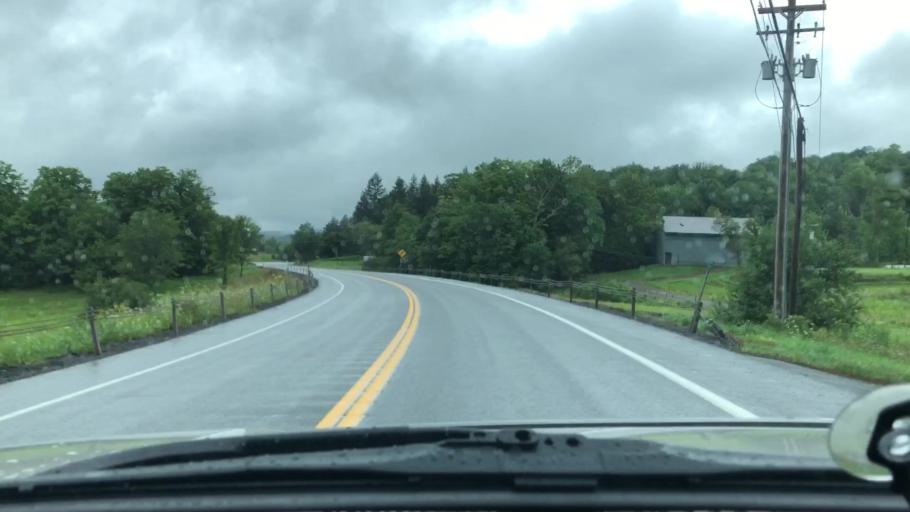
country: US
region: New York
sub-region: Greene County
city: Cairo
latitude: 42.3055
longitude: -74.2198
